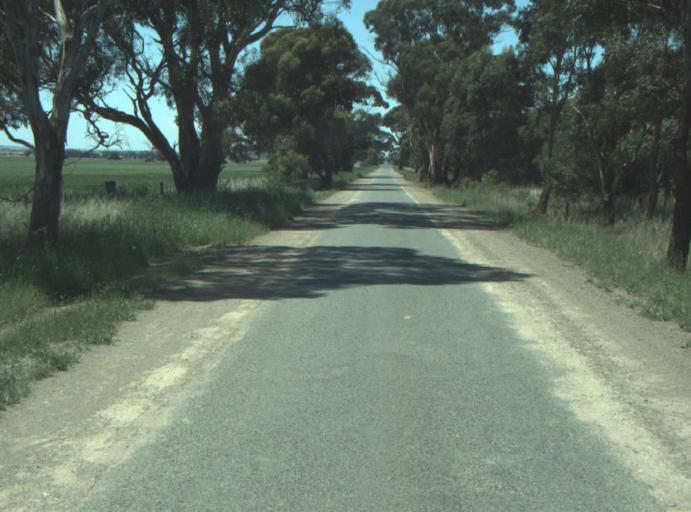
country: AU
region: Victoria
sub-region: Moorabool
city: Bacchus Marsh
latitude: -37.8273
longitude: 144.2988
